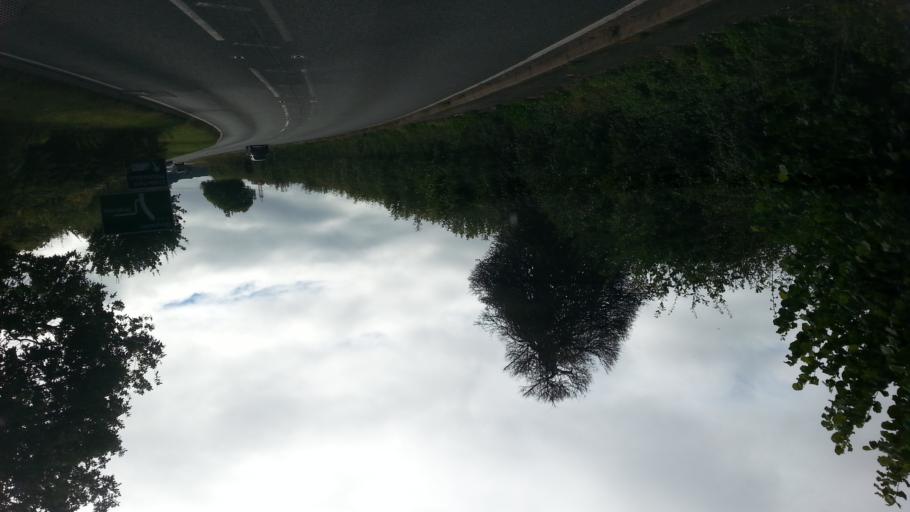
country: GB
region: England
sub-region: Herefordshire
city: Lea
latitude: 51.8981
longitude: -2.5207
